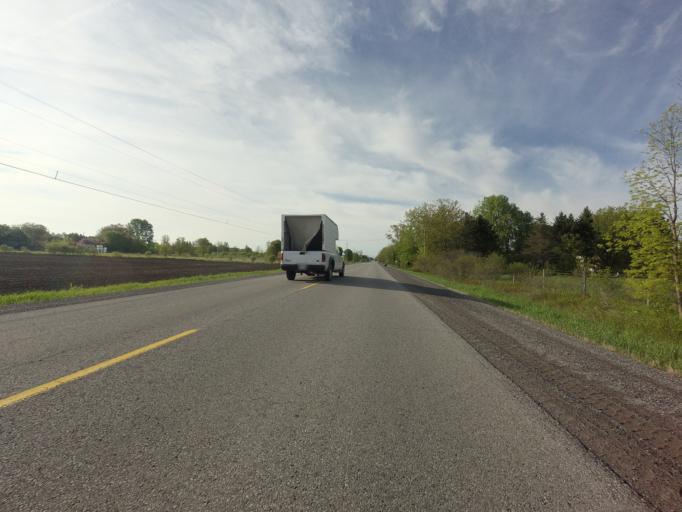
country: CA
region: Ontario
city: Ottawa
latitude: 45.2843
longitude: -75.4452
